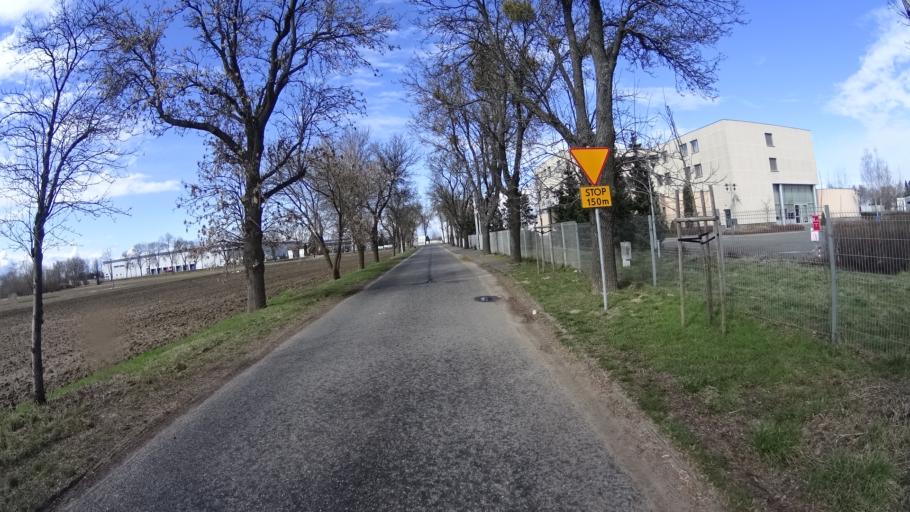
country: PL
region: Masovian Voivodeship
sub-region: Powiat warszawski zachodni
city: Jozefow
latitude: 52.2096
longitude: 20.6824
